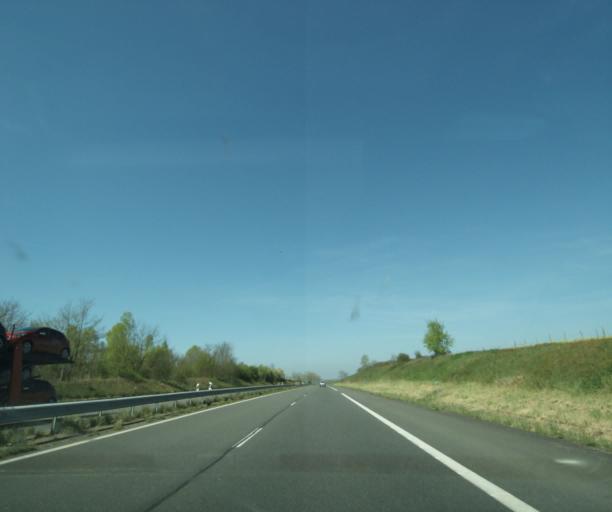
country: FR
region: Bourgogne
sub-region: Departement de la Nievre
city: Chaulgnes
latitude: 47.1159
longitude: 3.0618
